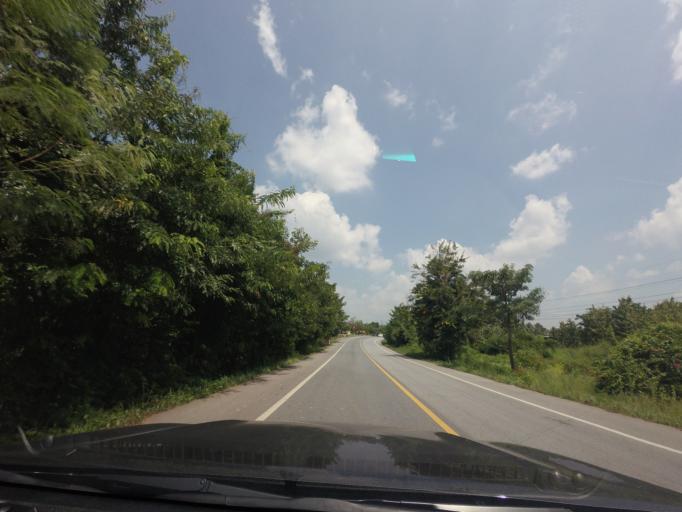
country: TH
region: Phitsanulok
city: Chat Trakan
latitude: 17.2982
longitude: 100.4151
